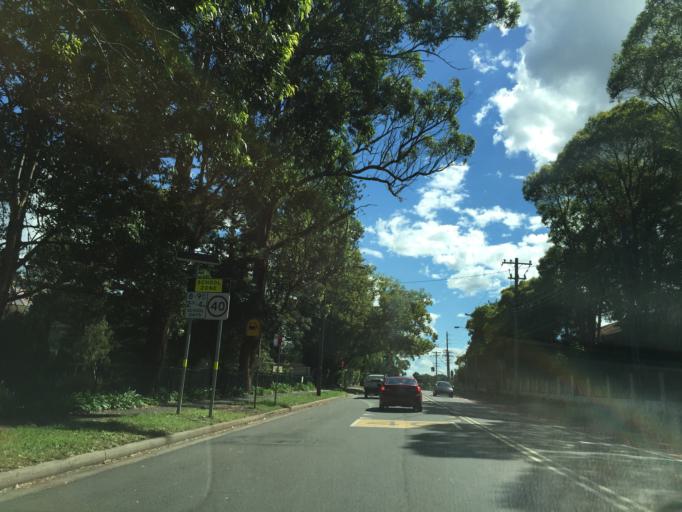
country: AU
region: New South Wales
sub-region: Ryde
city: Marsfield
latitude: -33.7795
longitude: 151.1043
